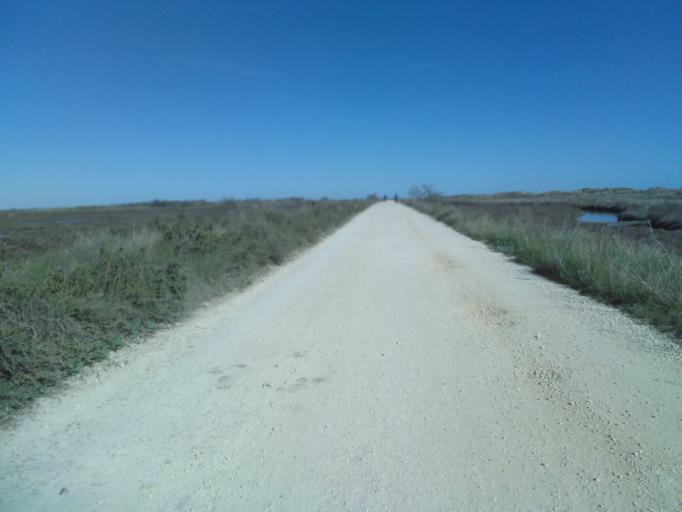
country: FR
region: Provence-Alpes-Cote d'Azur
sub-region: Departement des Bouches-du-Rhone
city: Saintes-Maries-de-la-Mer
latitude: 43.4604
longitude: 4.4880
